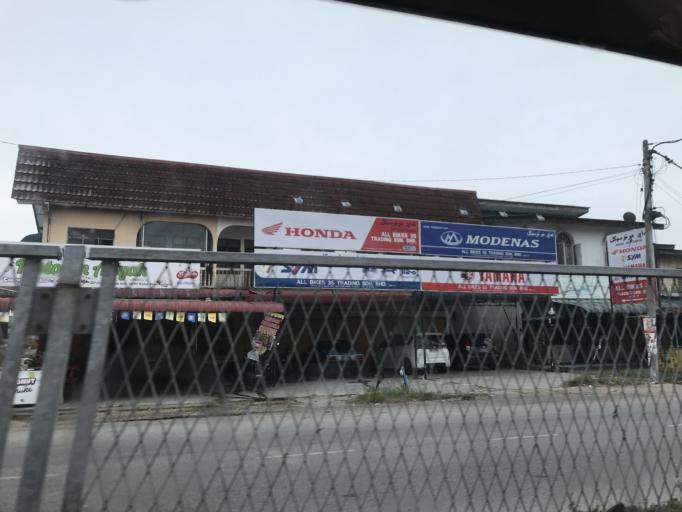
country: MY
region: Kelantan
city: Kota Bharu
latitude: 6.1197
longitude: 102.2150
